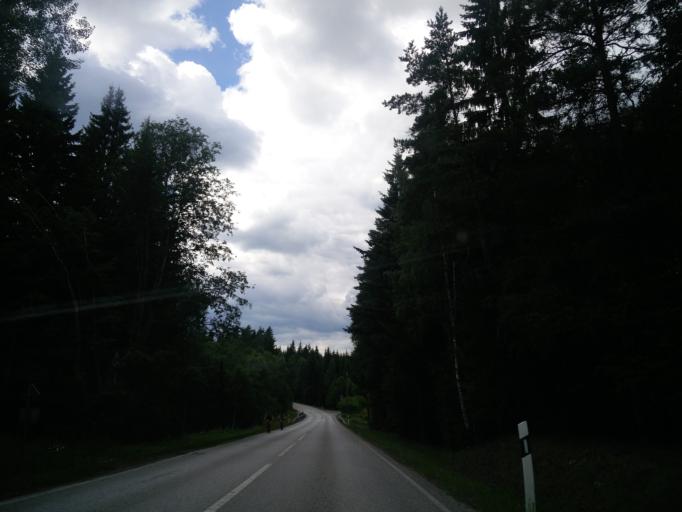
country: SE
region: OErebro
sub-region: Ljusnarsbergs Kommun
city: Kopparberg
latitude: 59.7901
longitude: 14.7661
